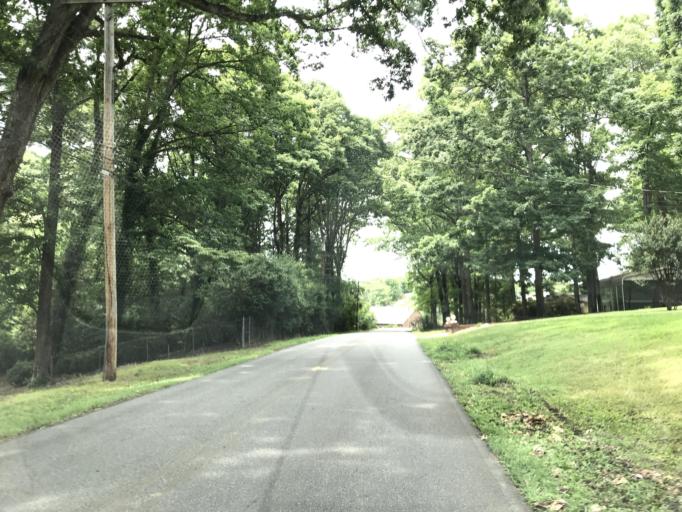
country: US
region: North Carolina
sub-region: Lincoln County
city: Lincolnton
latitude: 35.4814
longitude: -81.2516
